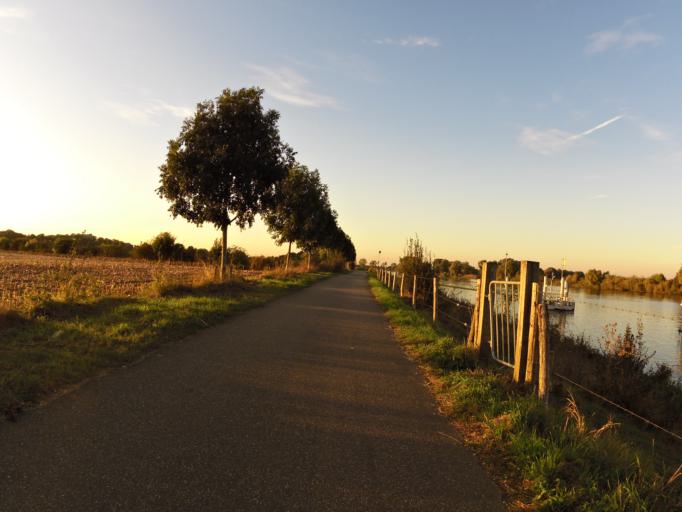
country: NL
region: North Brabant
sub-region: Gemeente Boxmeer
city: Boxmeer
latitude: 51.6432
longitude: 5.9728
